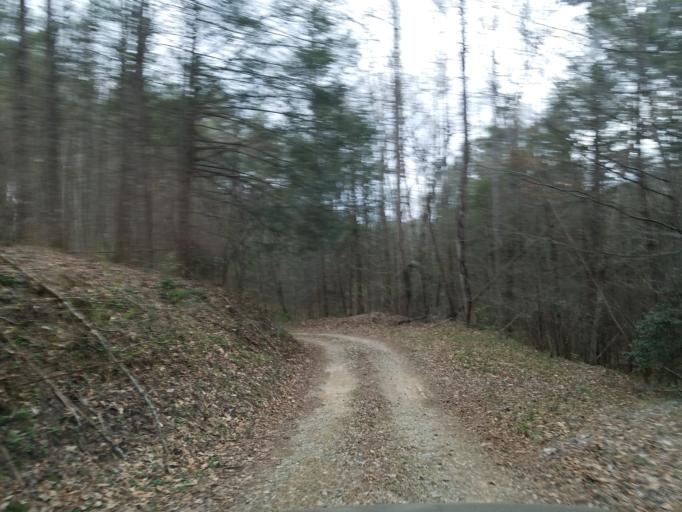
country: US
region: Georgia
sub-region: Union County
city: Blairsville
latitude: 34.7711
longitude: -84.0904
